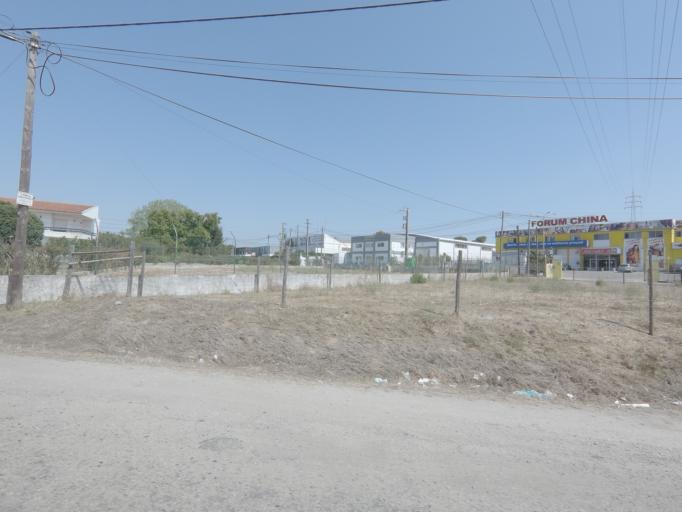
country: PT
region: Setubal
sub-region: Palmela
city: Palmela
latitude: 38.5522
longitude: -8.8857
